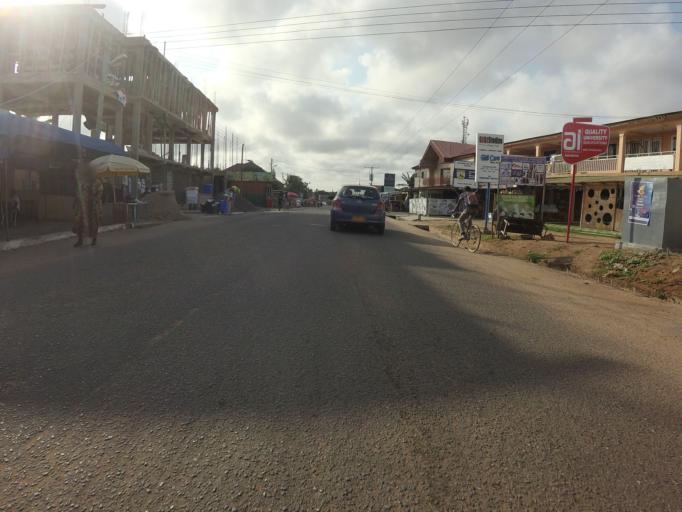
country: GH
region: Greater Accra
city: Nungua
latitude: 5.6158
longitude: -0.0763
